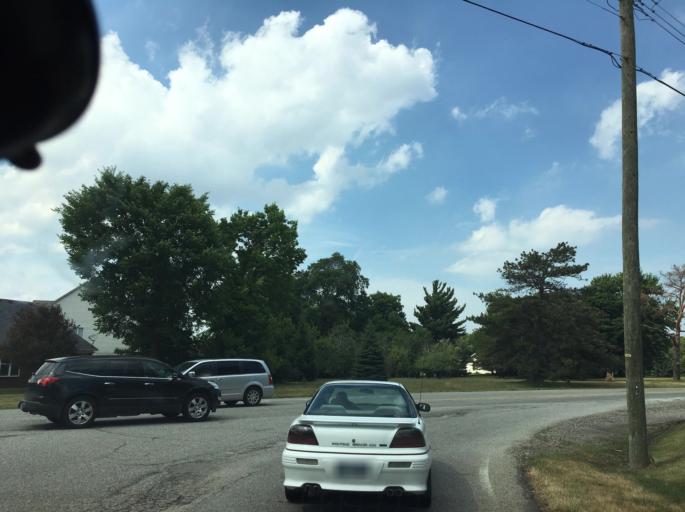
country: US
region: Michigan
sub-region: Macomb County
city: Fraser
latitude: 42.5576
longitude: -82.9704
